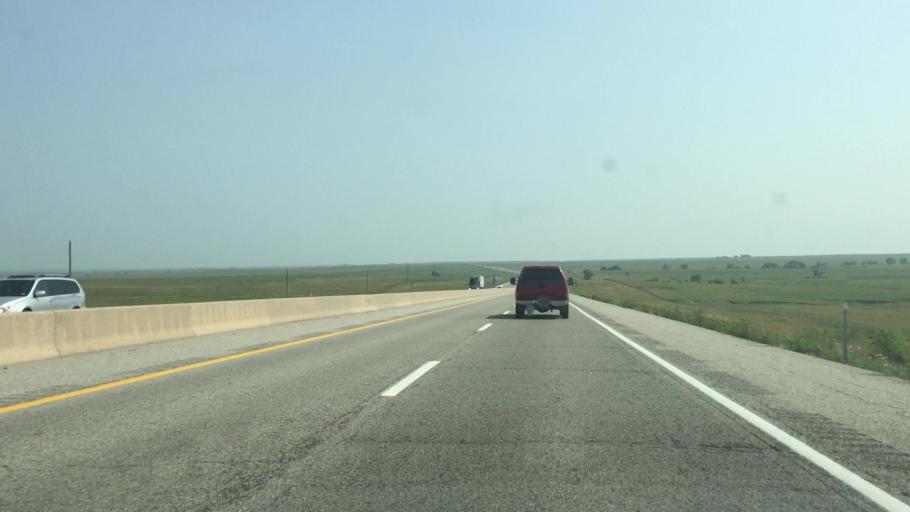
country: US
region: Kansas
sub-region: Chase County
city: Cottonwood Falls
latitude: 38.2783
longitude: -96.3707
